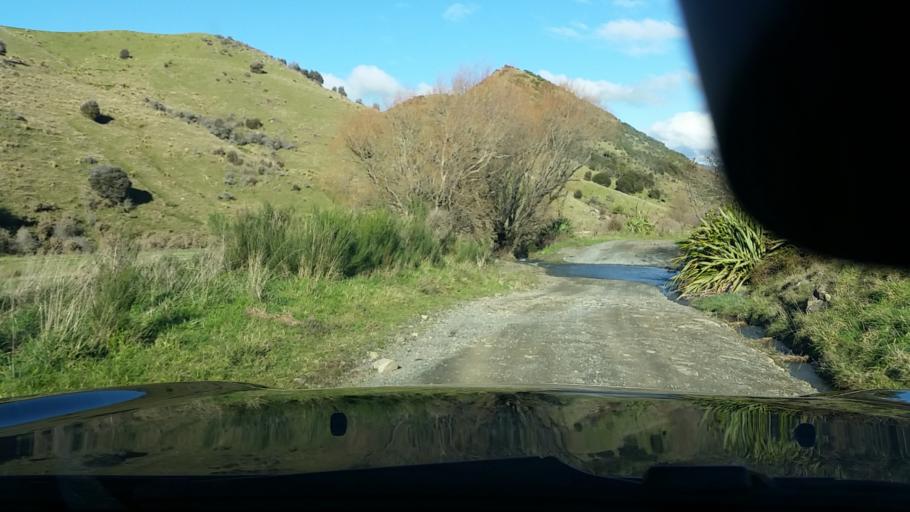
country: NZ
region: Marlborough
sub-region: Marlborough District
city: Blenheim
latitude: -41.6405
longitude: 173.9681
